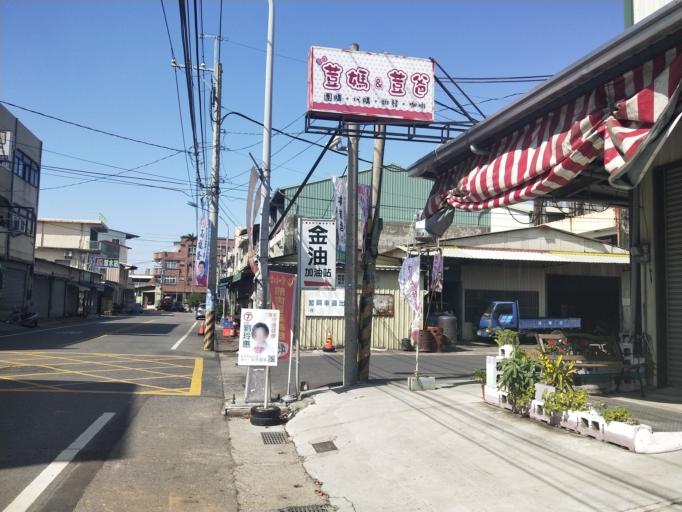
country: TW
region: Taiwan
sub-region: Changhua
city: Chang-hua
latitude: 24.0631
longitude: 120.5161
